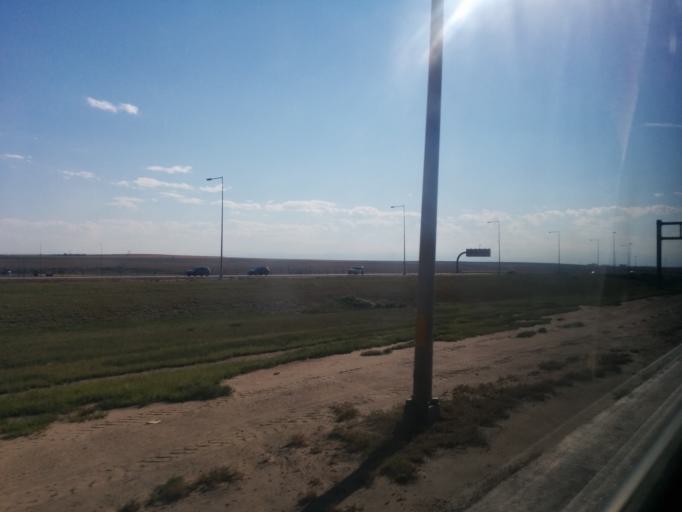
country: US
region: Colorado
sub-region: Adams County
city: Aurora
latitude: 39.8343
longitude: -104.7119
